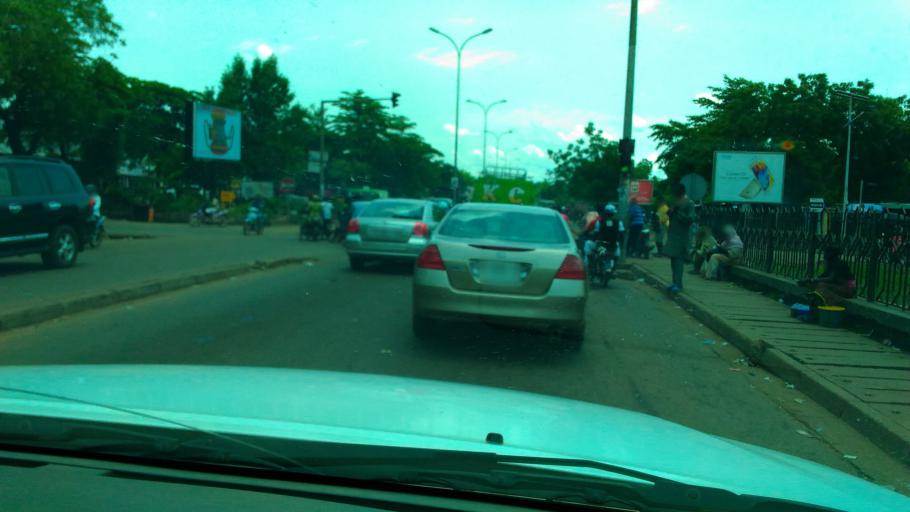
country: ML
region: Bamako
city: Bamako
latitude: 12.6531
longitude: -7.9821
